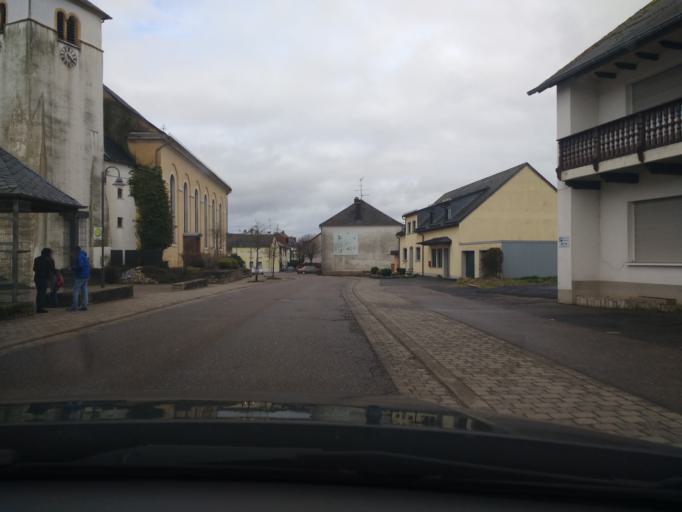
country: DE
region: Rheinland-Pfalz
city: Schillingen
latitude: 49.6346
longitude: 6.7861
